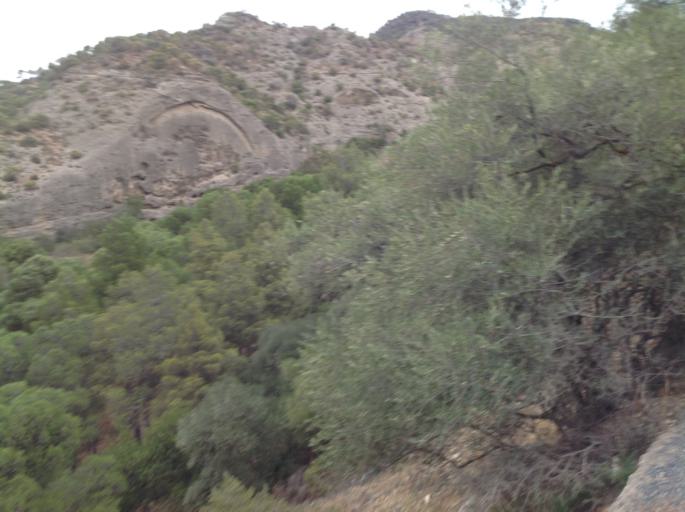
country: ES
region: Andalusia
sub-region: Provincia de Malaga
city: Ardales
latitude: 36.9297
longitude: -4.7924
